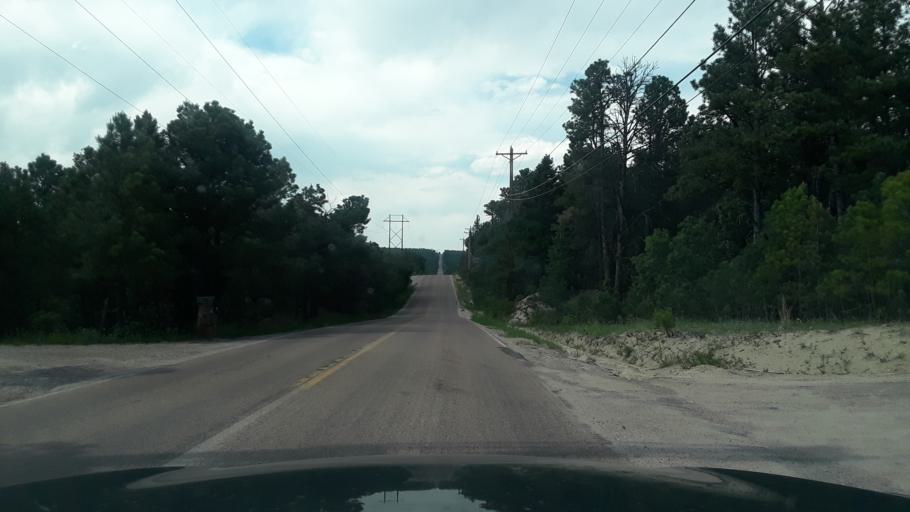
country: US
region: Colorado
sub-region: El Paso County
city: Gleneagle
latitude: 39.0480
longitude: -104.7848
